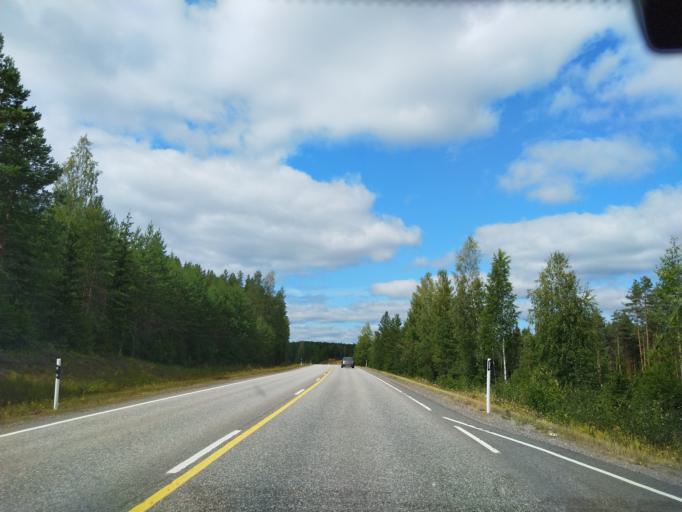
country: FI
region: Haeme
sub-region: Riihimaeki
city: Loppi
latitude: 60.7354
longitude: 24.3824
